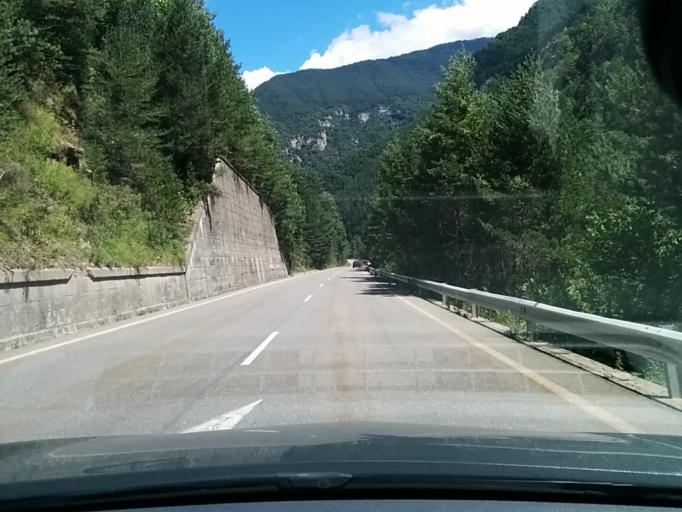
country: ES
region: Aragon
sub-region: Provincia de Huesca
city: Bielsa
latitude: 42.5929
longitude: 0.2345
